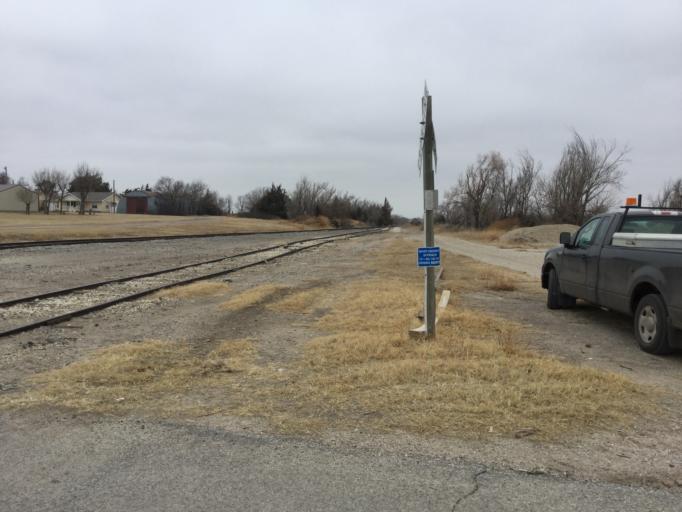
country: US
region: Kansas
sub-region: Edwards County
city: Kinsley
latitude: 38.1925
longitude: -99.5284
